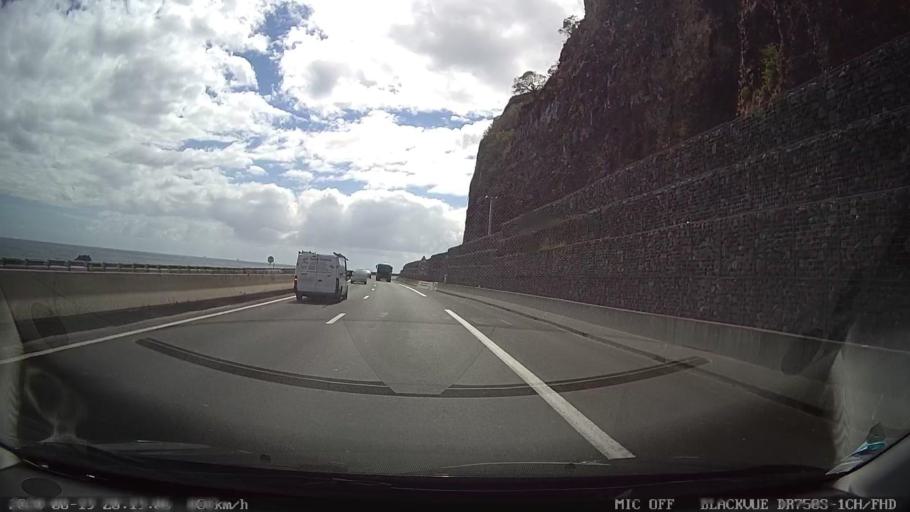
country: RE
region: Reunion
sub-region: Reunion
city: La Possession
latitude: -20.9139
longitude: 55.3501
